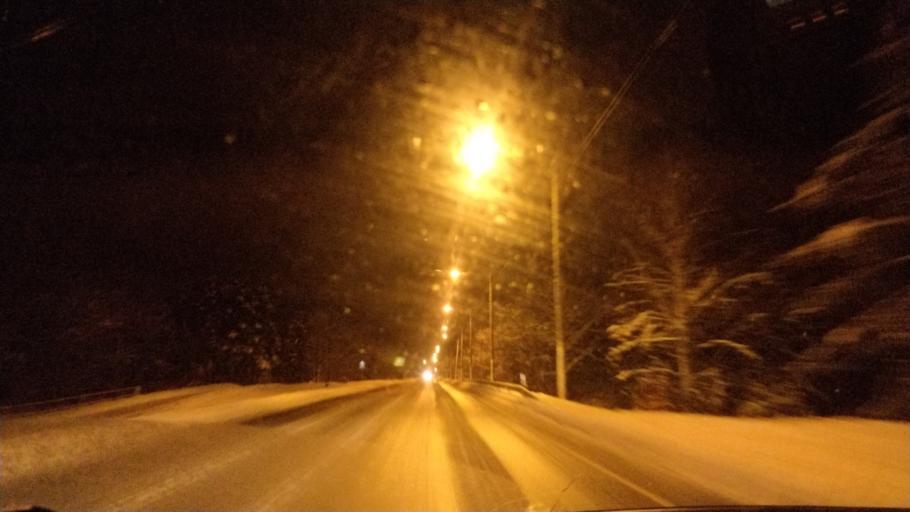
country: FI
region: Lapland
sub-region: Rovaniemi
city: Rovaniemi
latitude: 66.2664
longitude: 25.3342
